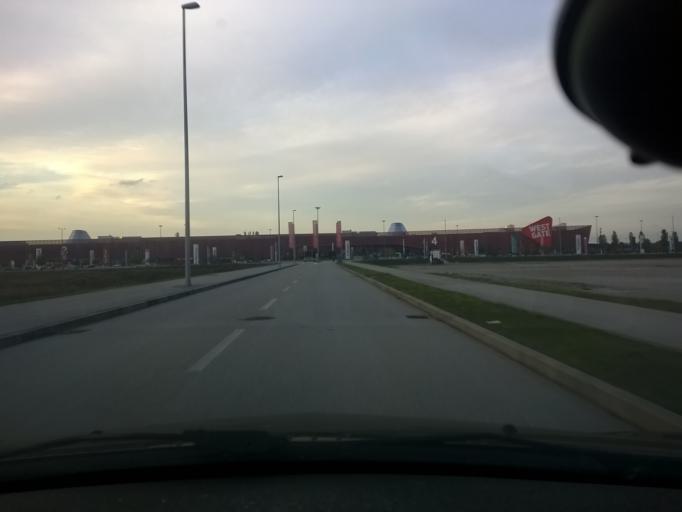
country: HR
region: Zagrebacka
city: Zapresic
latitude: 45.8679
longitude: 15.8282
